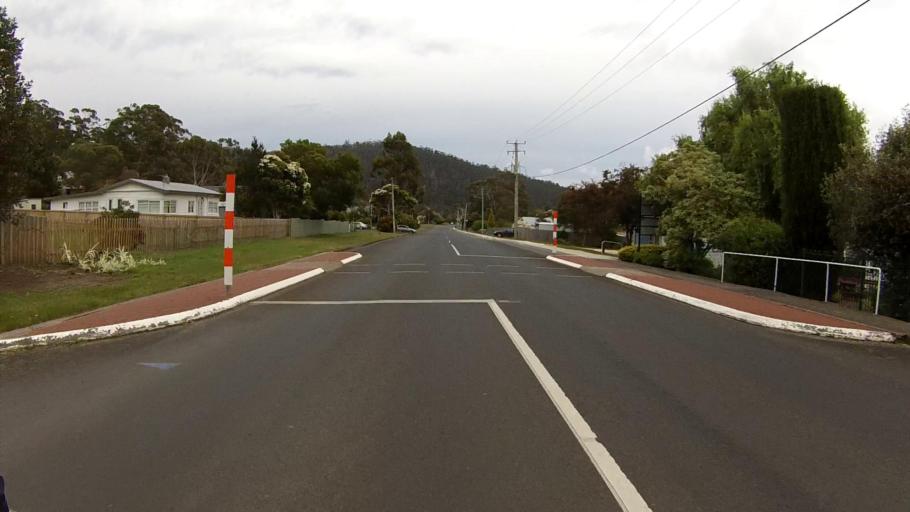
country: AU
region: Tasmania
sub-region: Sorell
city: Sorell
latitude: -42.5632
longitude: 147.8729
